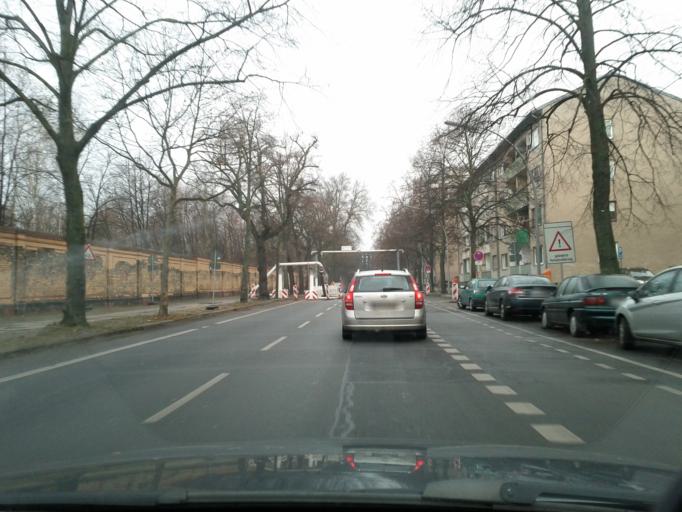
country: DE
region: Berlin
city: Gesundbrunnen
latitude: 52.5380
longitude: 13.3820
